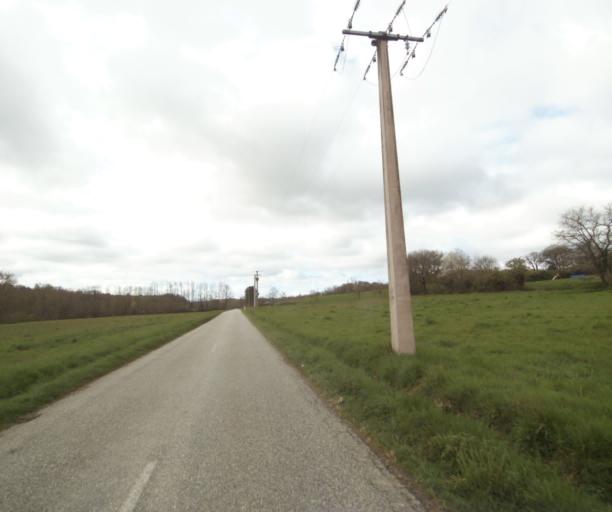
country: FR
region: Midi-Pyrenees
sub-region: Departement de l'Ariege
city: Saverdun
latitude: 43.2187
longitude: 1.5297
